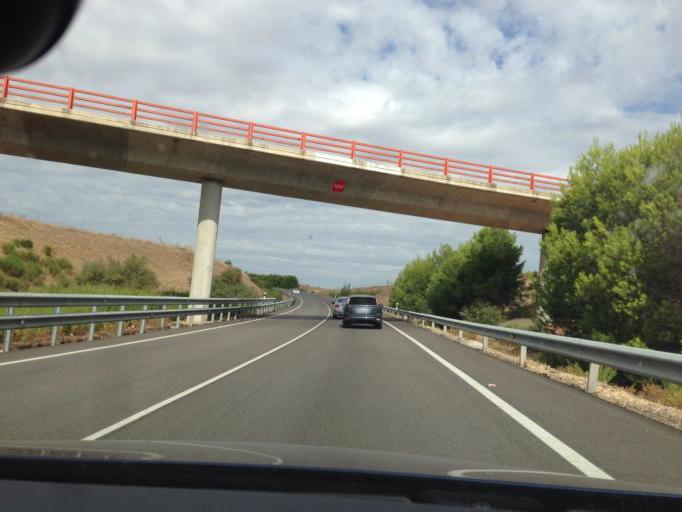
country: ES
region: Madrid
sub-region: Provincia de Madrid
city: Daganzo de Arriba
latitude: 40.5319
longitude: -3.4275
